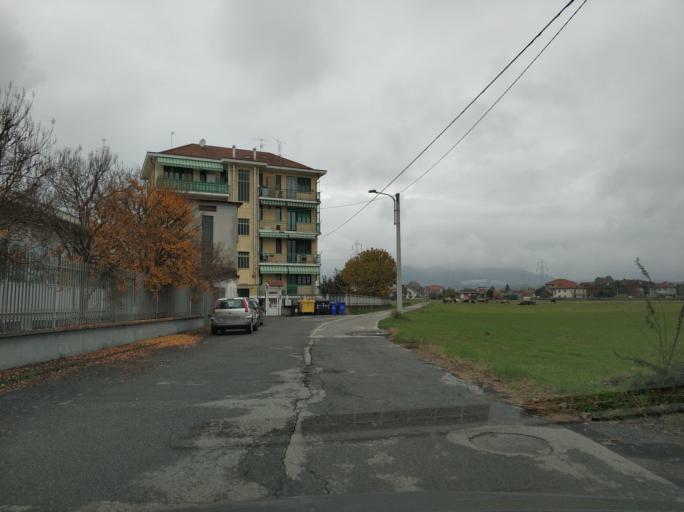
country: IT
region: Piedmont
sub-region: Provincia di Torino
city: Villanova Canavese
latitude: 45.2481
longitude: 7.5511
